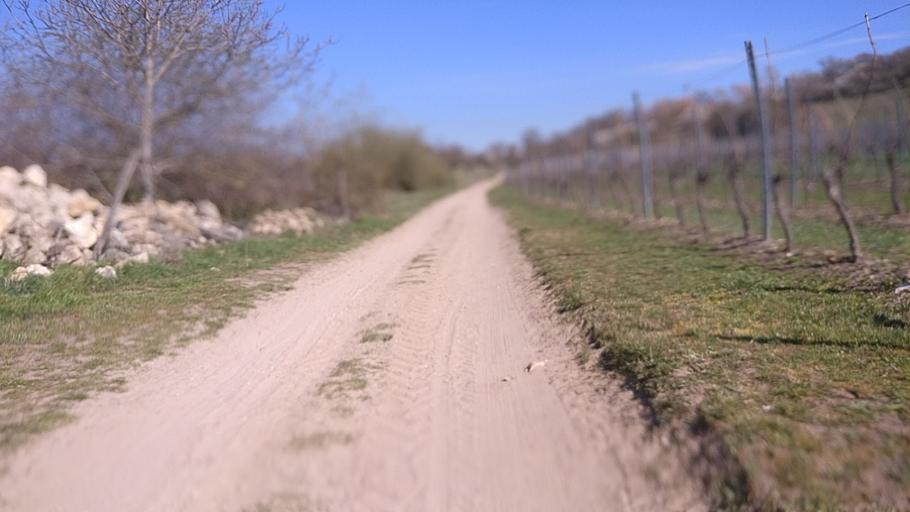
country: DE
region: Rheinland-Pfalz
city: Gau-Algesheim
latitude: 49.9627
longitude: 8.0240
